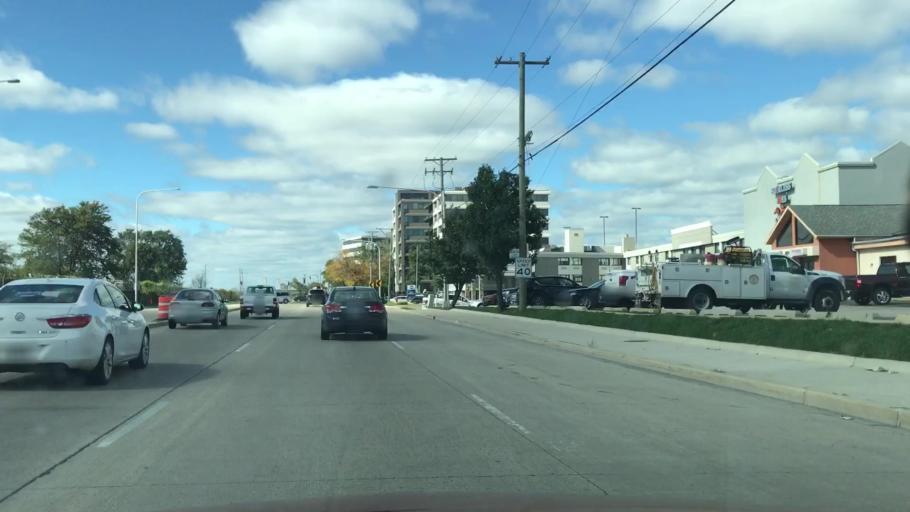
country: US
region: Illinois
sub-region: Cook County
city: Rosemont
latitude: 41.9984
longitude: -87.8850
